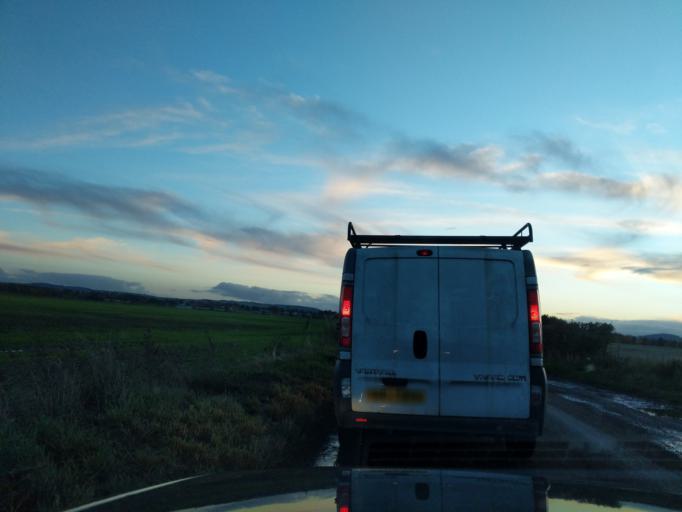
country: GB
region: Scotland
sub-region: Fife
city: Leuchars
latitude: 56.3965
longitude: -2.8665
